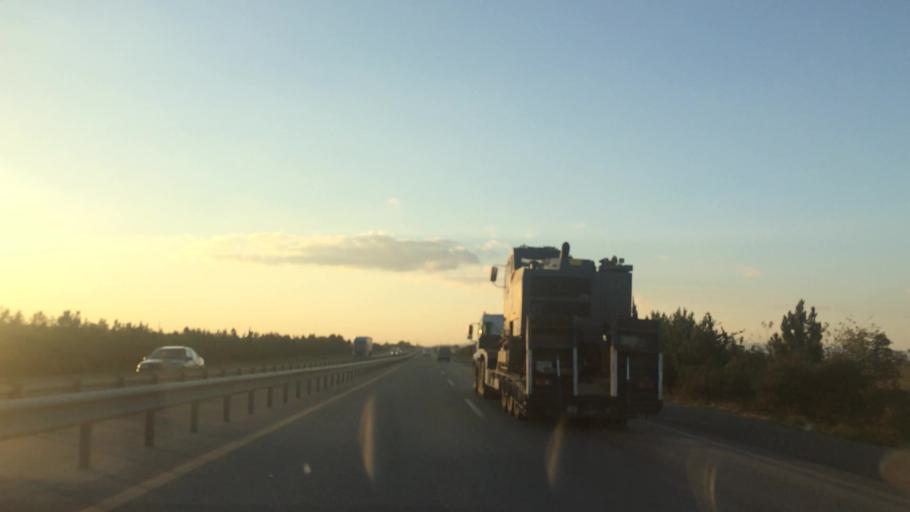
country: AZ
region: Haciqabul
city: Haciqabul
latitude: 40.0229
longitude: 49.1190
